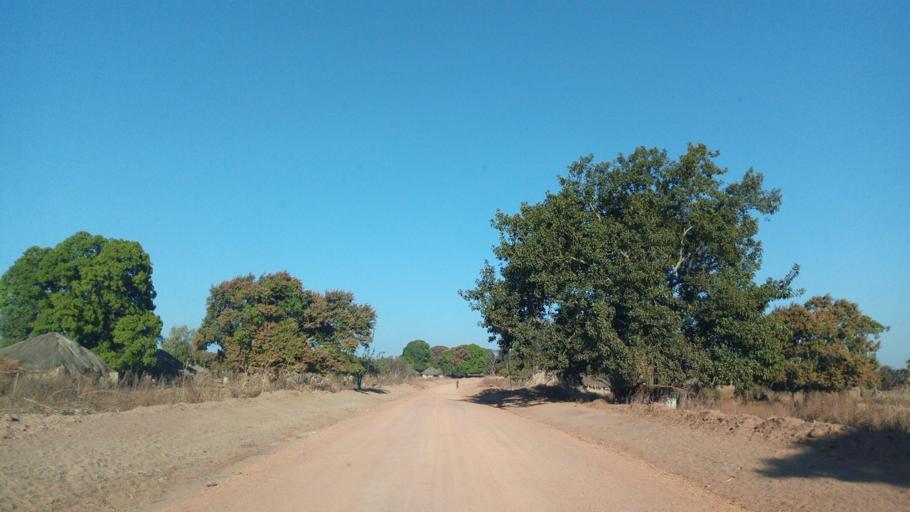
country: ZM
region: Luapula
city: Mwense
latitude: -10.4444
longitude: 28.5780
